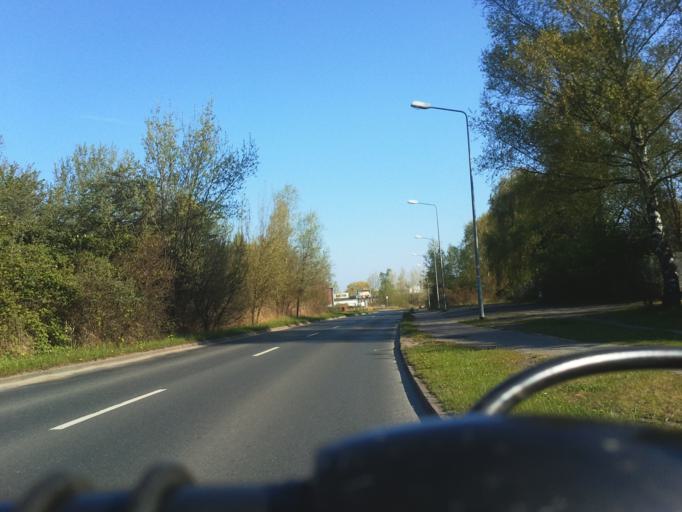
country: DE
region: Mecklenburg-Vorpommern
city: Rostock
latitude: 54.1039
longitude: 12.0918
